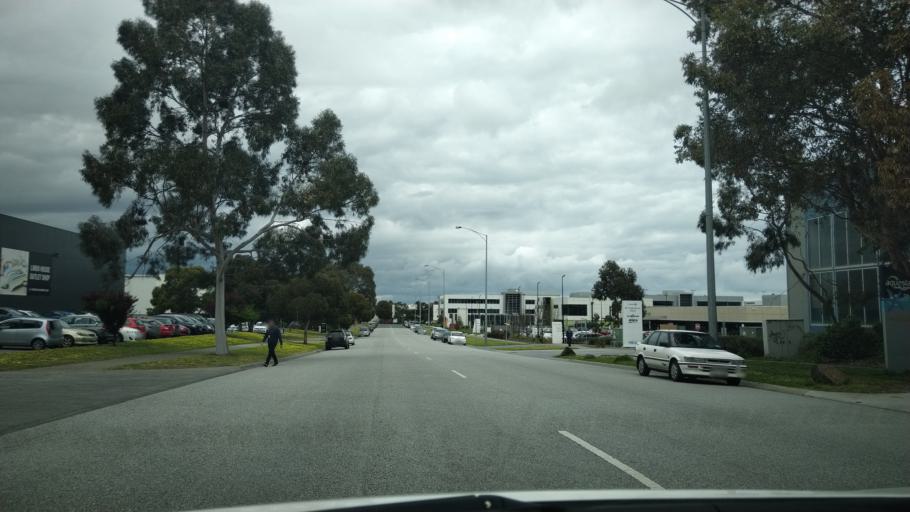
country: AU
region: Victoria
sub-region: Monash
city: Oakleigh South
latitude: -37.9477
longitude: 145.0815
